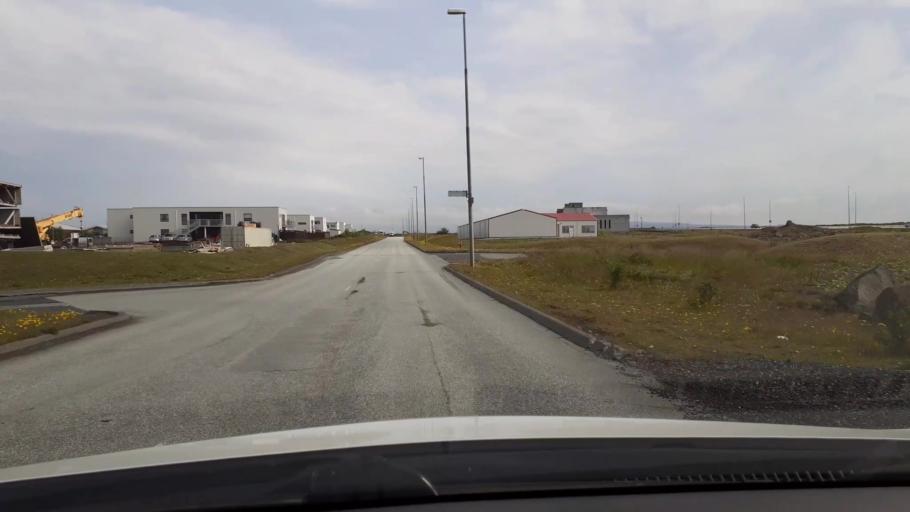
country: IS
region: Southern Peninsula
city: Reykjanesbaer
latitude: 63.9715
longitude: -22.5239
